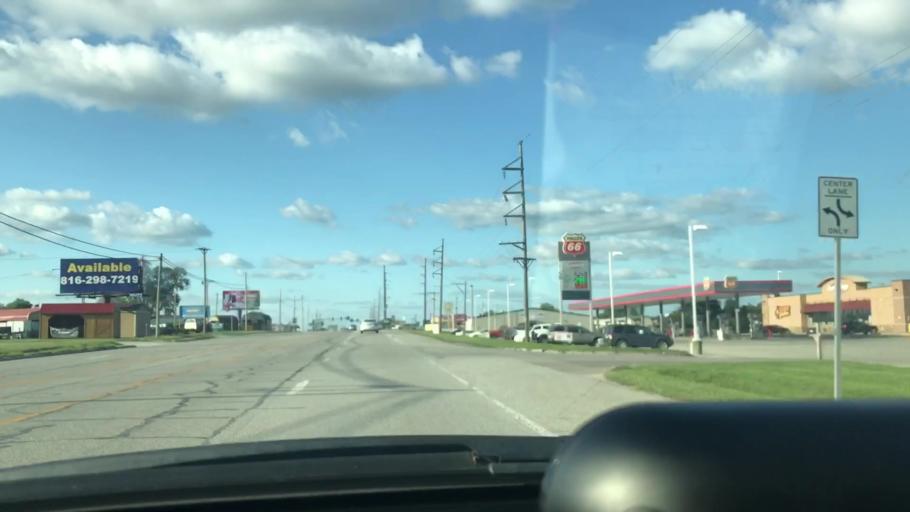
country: US
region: Missouri
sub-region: Pettis County
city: Sedalia
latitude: 38.6710
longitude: -93.2518
